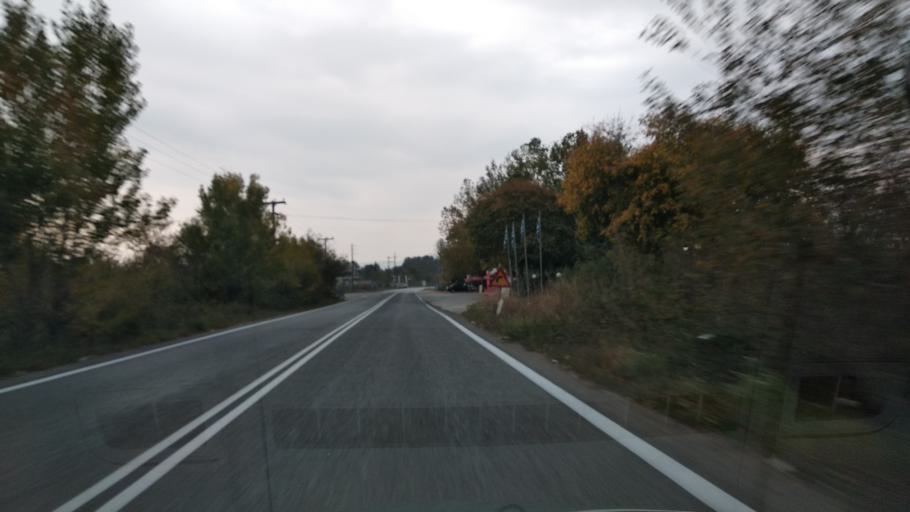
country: GR
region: Thessaly
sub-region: Trikala
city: Pyrgetos
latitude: 39.5271
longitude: 21.7352
